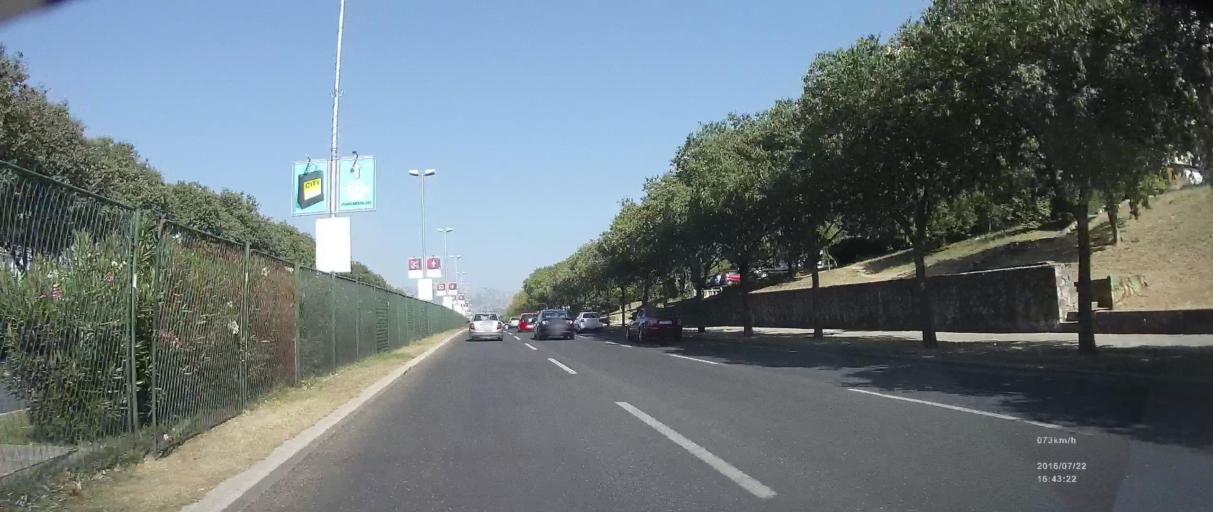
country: HR
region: Splitsko-Dalmatinska
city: Vranjic
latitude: 43.5195
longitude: 16.4686
